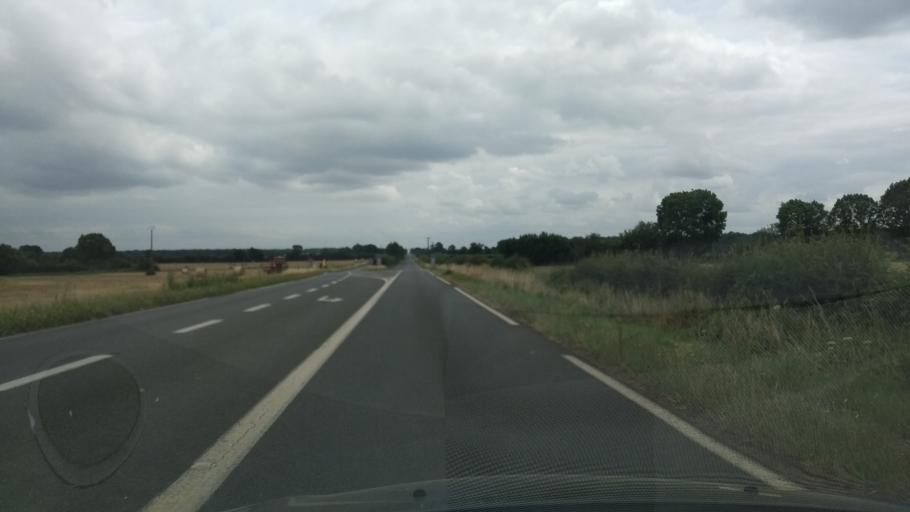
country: FR
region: Poitou-Charentes
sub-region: Departement de la Vienne
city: La Villedieu-du-Clain
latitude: 46.4262
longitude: 0.3789
